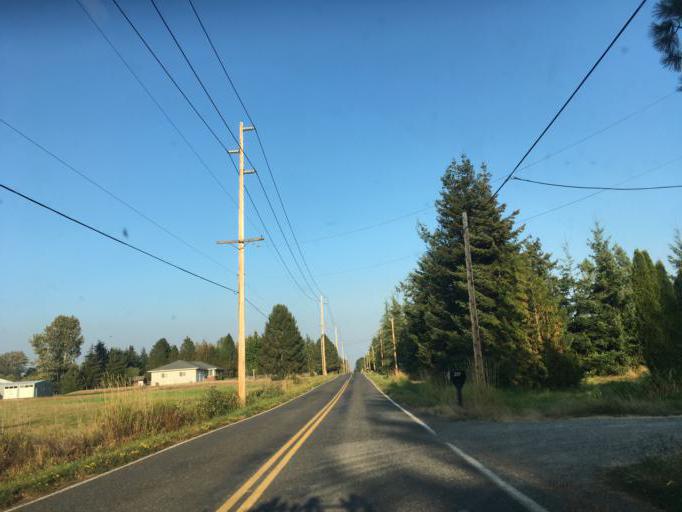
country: US
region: Washington
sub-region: Whatcom County
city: Bellingham
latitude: 48.8151
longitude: -122.4815
